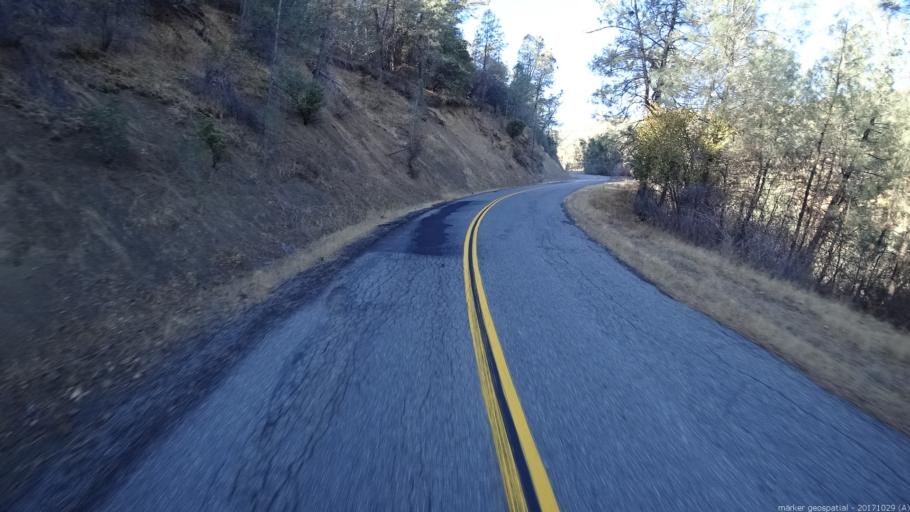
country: US
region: California
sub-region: Trinity County
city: Lewiston
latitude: 40.3861
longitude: -122.8317
